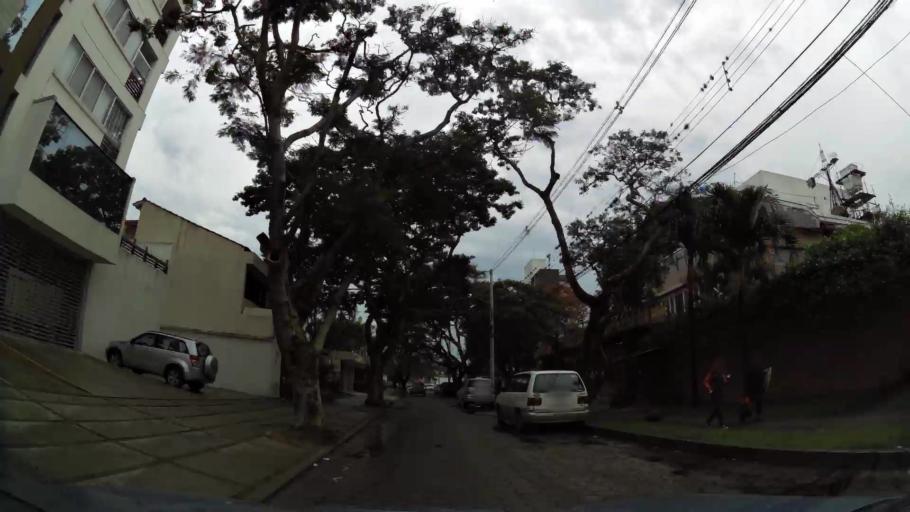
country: BO
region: Santa Cruz
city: Santa Cruz de la Sierra
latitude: -17.7932
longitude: -63.1786
